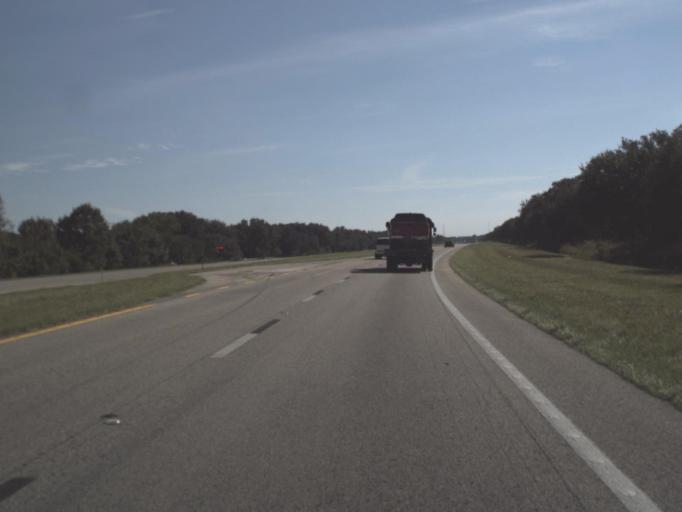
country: US
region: Florida
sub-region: Hendry County
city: Port LaBelle
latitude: 26.9690
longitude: -81.3167
